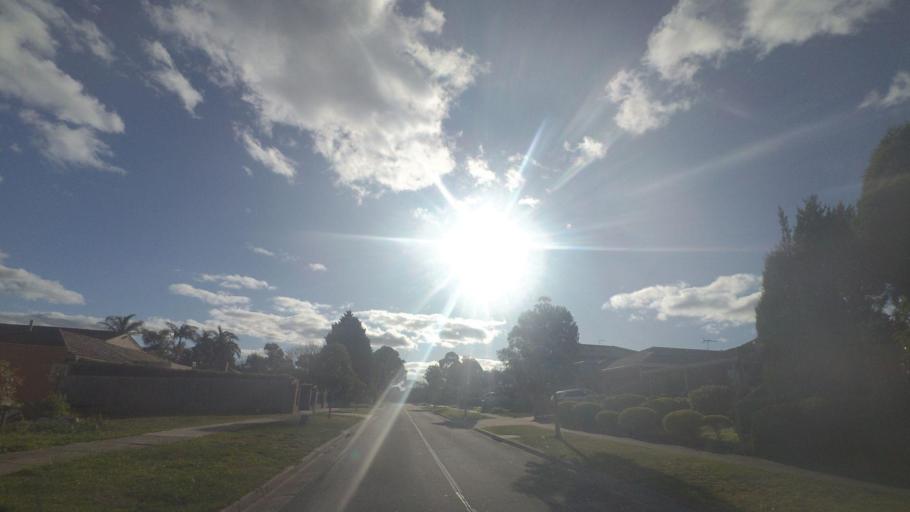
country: AU
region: Victoria
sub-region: Knox
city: Ferntree Gully
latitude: -37.9099
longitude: 145.2786
